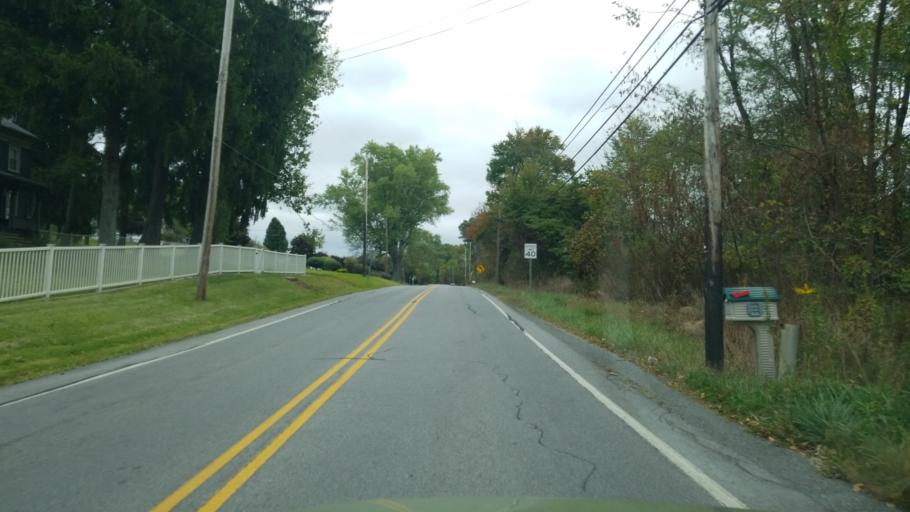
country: US
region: Pennsylvania
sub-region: Clearfield County
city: Hyde
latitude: 40.9921
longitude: -78.4701
